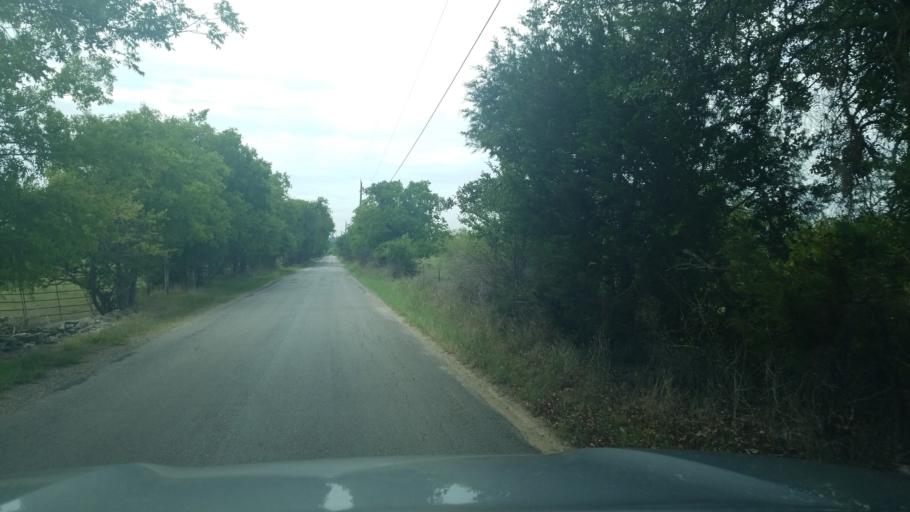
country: US
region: Texas
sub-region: Comal County
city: Bulverde
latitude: 29.7523
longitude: -98.4110
